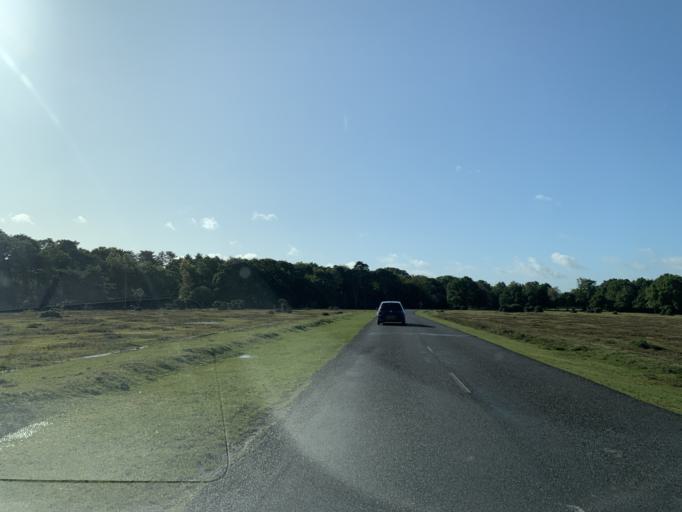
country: GB
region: England
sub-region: Hampshire
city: Cadnam
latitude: 50.9331
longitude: -1.6544
